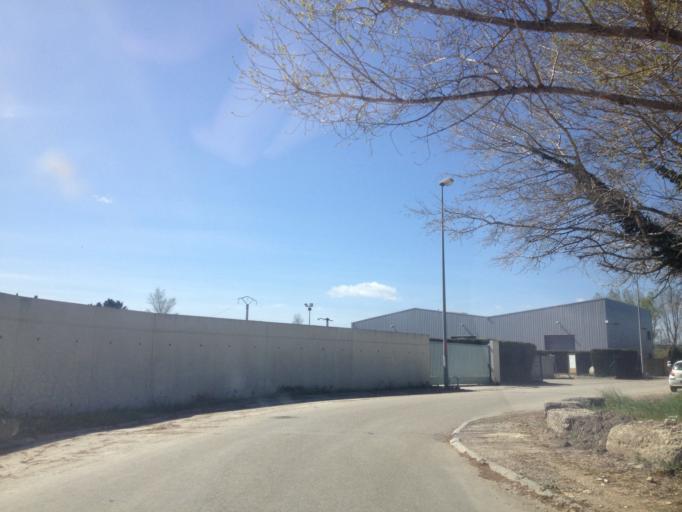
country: FR
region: Languedoc-Roussillon
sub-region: Departement du Gard
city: Les Angles
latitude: 43.9309
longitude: 4.7721
